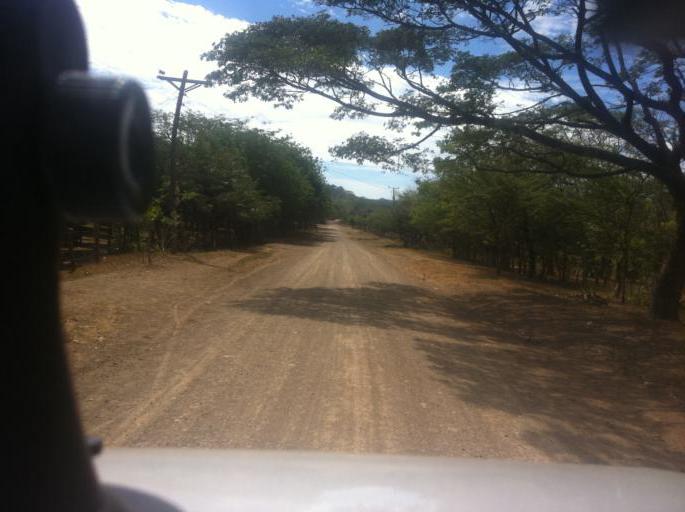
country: NI
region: Granada
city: Nandaime
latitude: 11.6184
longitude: -86.0274
